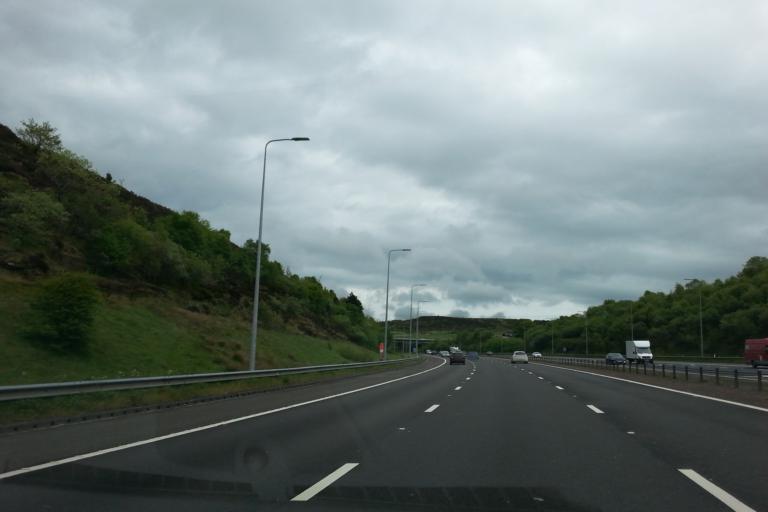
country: GB
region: England
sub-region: Kirklees
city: Marsden
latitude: 53.6446
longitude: -1.9017
